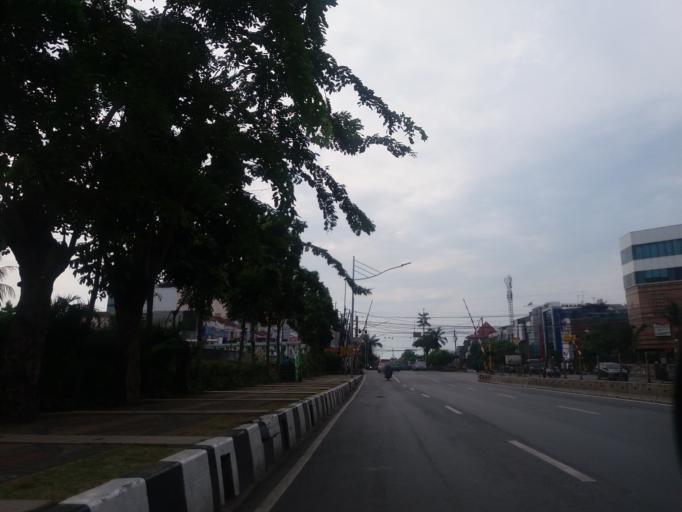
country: ID
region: Jakarta Raya
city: Jakarta
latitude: -6.1424
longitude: 106.8335
